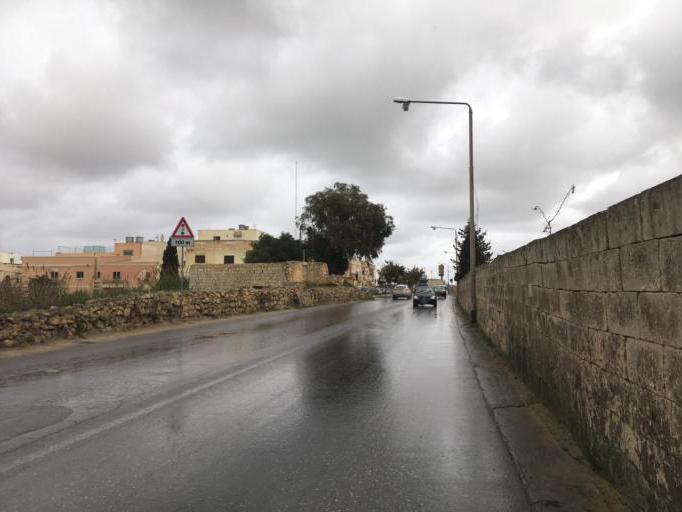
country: MT
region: Hal Gharghur
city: Hal Gharghur
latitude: 35.9164
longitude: 14.4523
